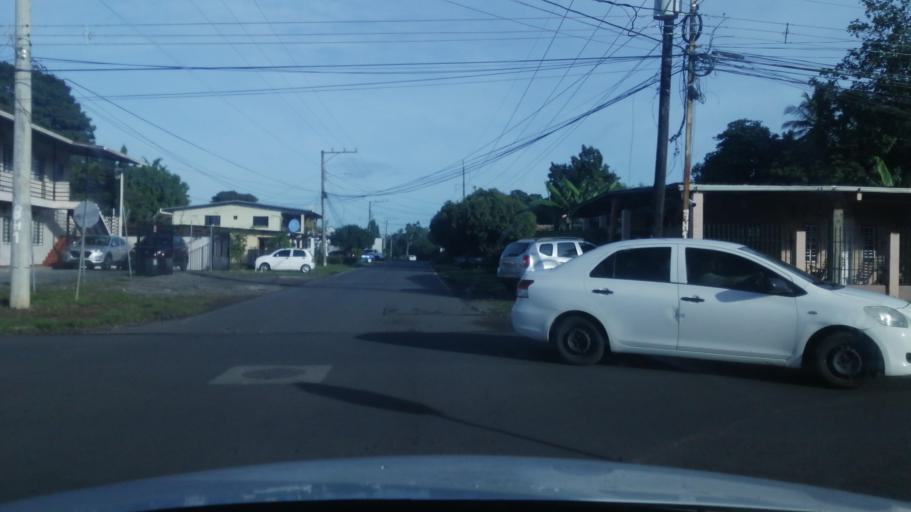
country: PA
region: Chiriqui
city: David
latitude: 8.4232
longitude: -82.4364
